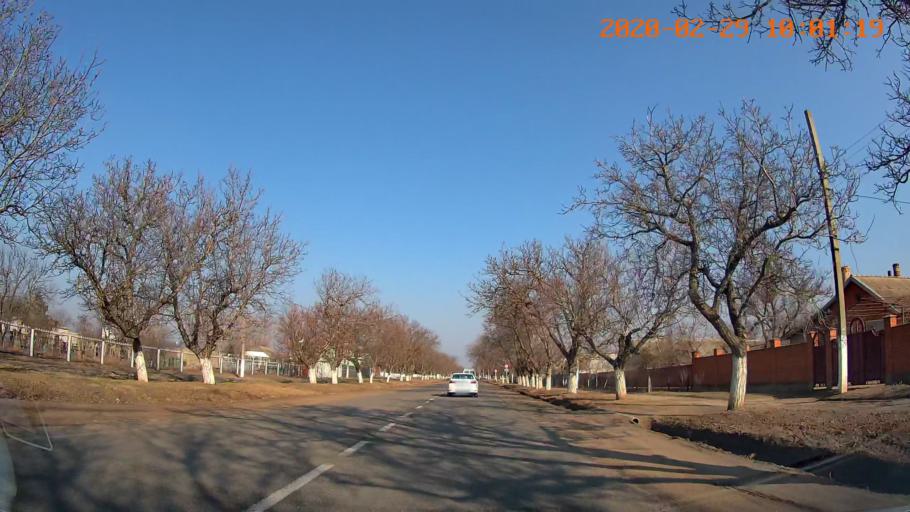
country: MD
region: Telenesti
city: Slobozia
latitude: 46.7744
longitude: 29.6848
